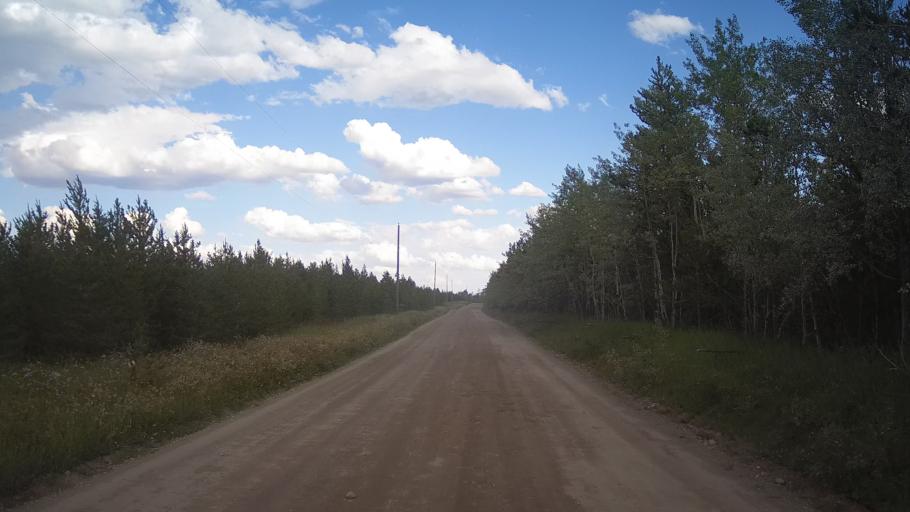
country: CA
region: British Columbia
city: Cache Creek
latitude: 51.2697
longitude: -121.7173
